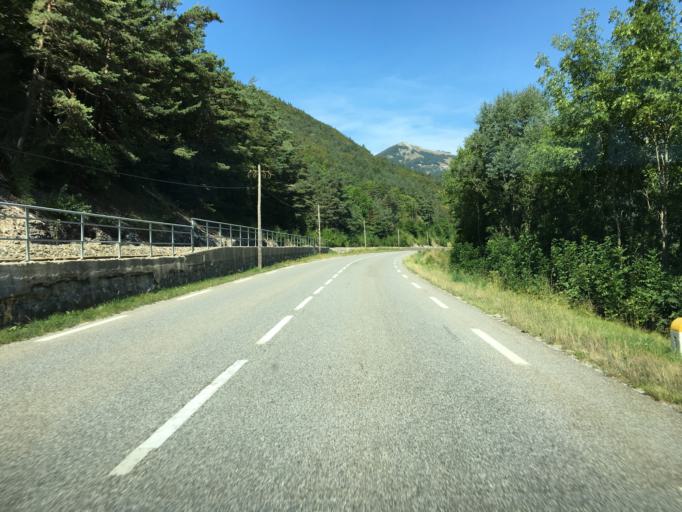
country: FR
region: Provence-Alpes-Cote d'Azur
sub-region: Departement des Hautes-Alpes
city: Veynes
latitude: 44.6501
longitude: 5.6981
